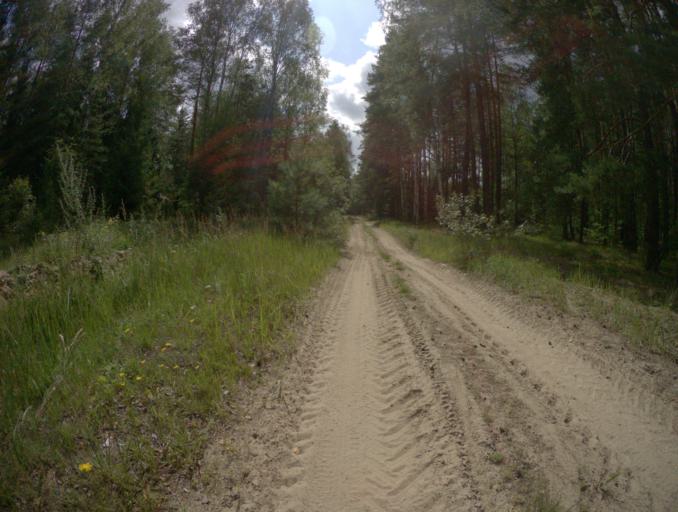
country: RU
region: Vladimir
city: Vorsha
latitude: 55.9621
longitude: 40.1562
